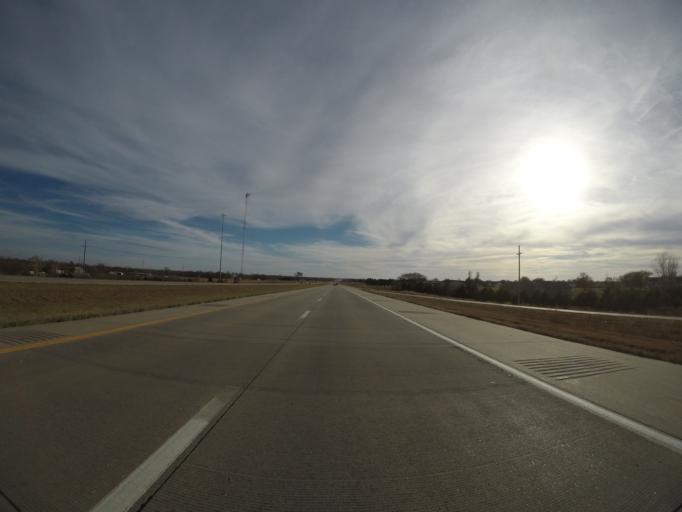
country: US
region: Kansas
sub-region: Franklin County
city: Ottawa
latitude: 38.6212
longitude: -95.2325
